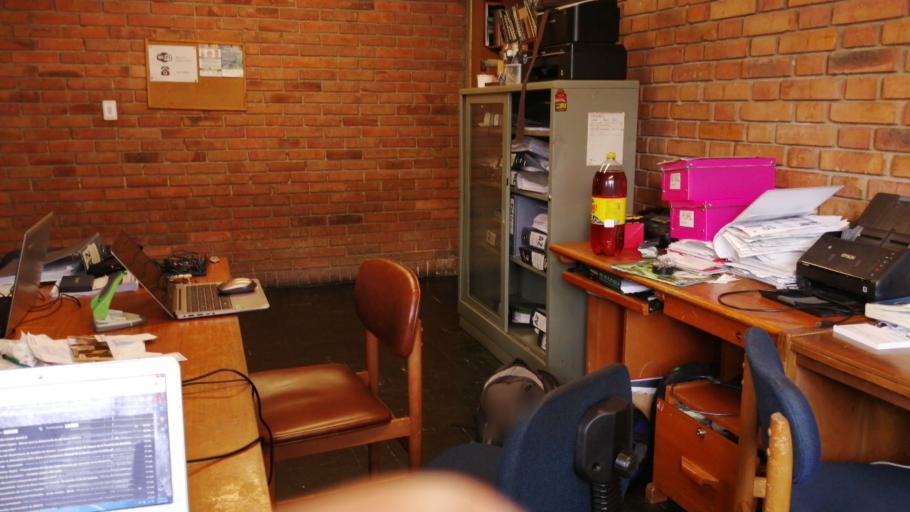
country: CO
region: Bogota D.C.
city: Bogota
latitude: 4.6407
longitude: -74.0907
